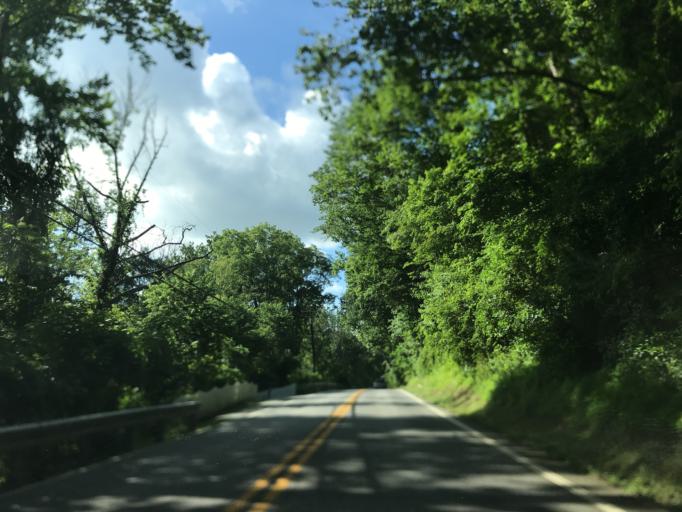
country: US
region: Maryland
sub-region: Carroll County
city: Hampstead
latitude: 39.5552
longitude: -76.7449
